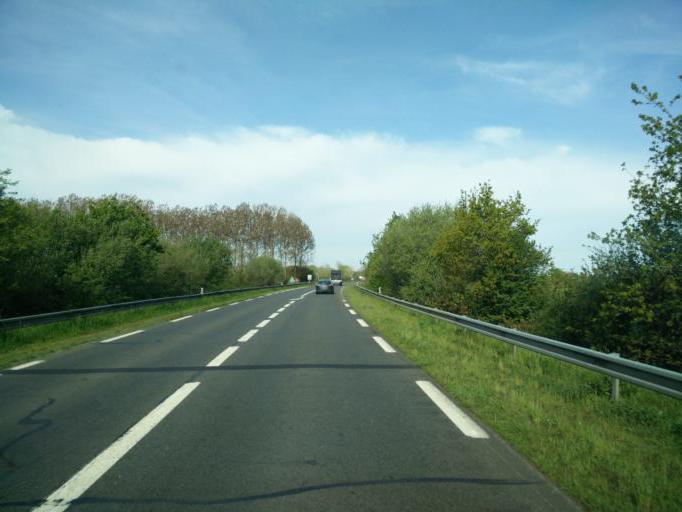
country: FR
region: Lower Normandy
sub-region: Departement de la Manche
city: Pontorson
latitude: 48.5605
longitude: -1.4924
